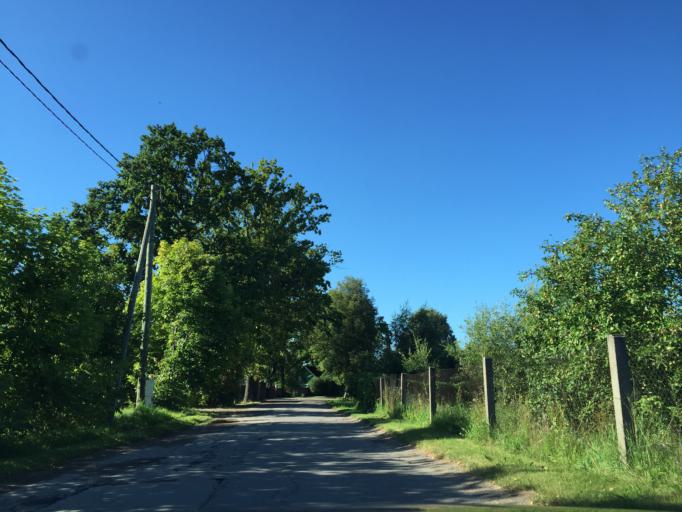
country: LV
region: Riga
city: Jaunciems
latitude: 57.0536
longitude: 24.1378
